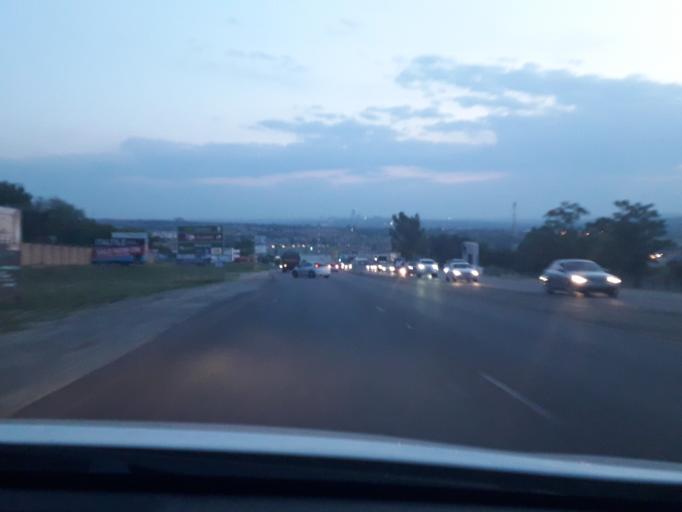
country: ZA
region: Gauteng
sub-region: City of Johannesburg Metropolitan Municipality
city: Midrand
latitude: -25.9951
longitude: 28.0763
